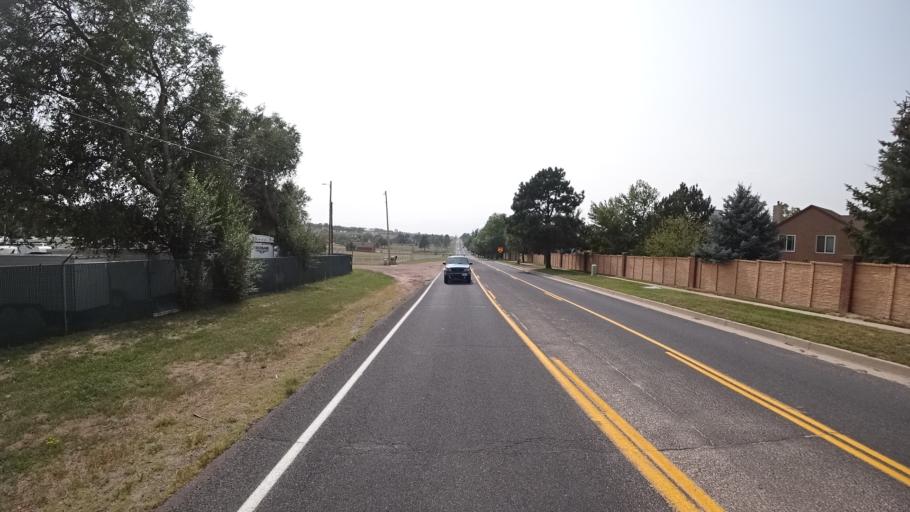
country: US
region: Colorado
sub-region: El Paso County
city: Cimarron Hills
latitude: 38.9206
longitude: -104.7221
